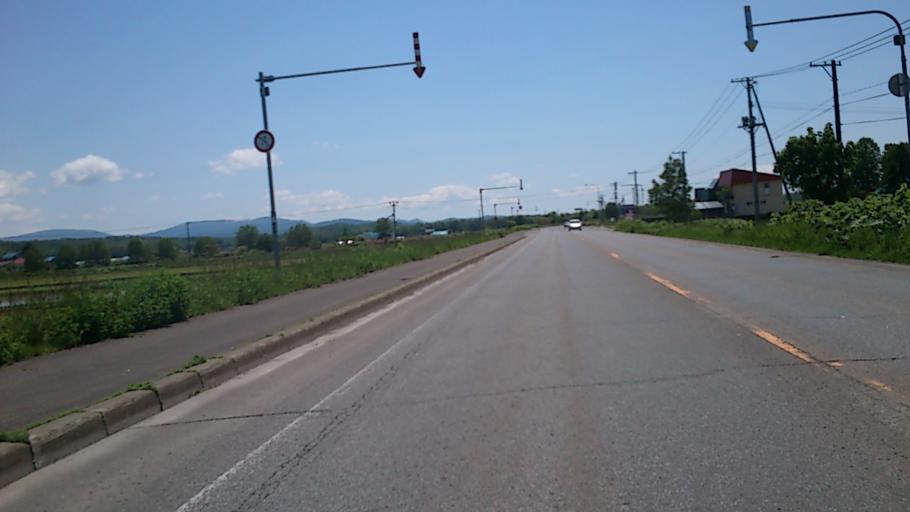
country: JP
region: Hokkaido
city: Nayoro
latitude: 44.3183
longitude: 142.4573
